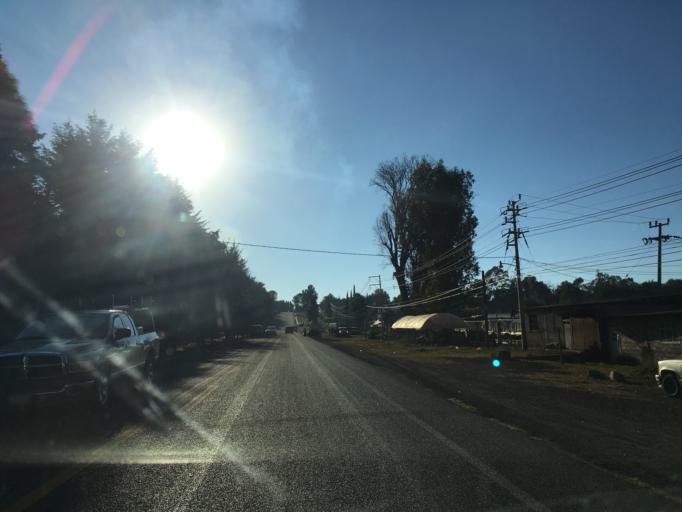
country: MX
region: Michoacan
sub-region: Zitacuaro
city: San Felipe los Alzati (Colonia Nueva)
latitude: 19.4873
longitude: -100.3832
